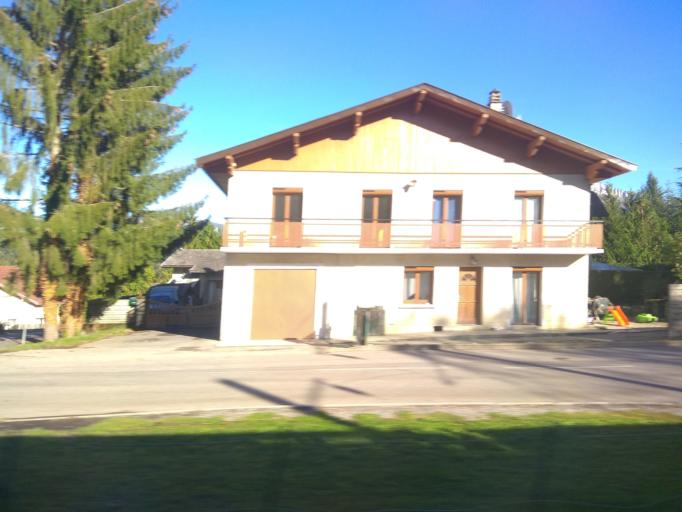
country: FR
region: Rhone-Alpes
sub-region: Departement de la Haute-Savoie
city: Saint-Martin-Bellevue
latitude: 45.9669
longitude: 6.1577
